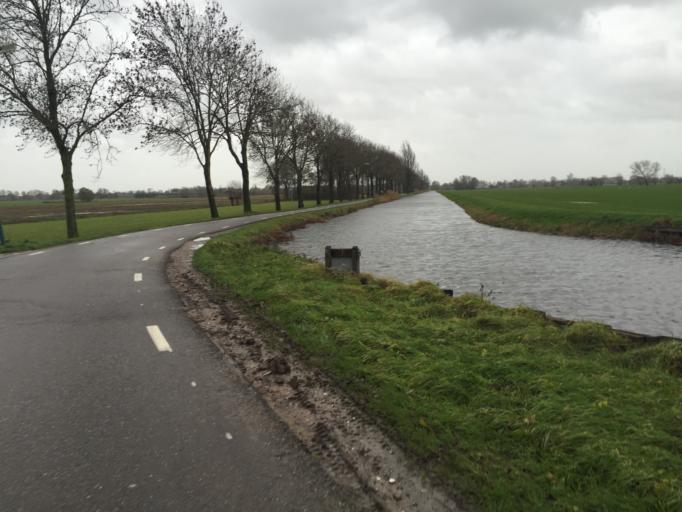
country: NL
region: Utrecht
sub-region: Gemeente Montfoort
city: Montfoort
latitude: 52.0598
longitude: 4.9408
